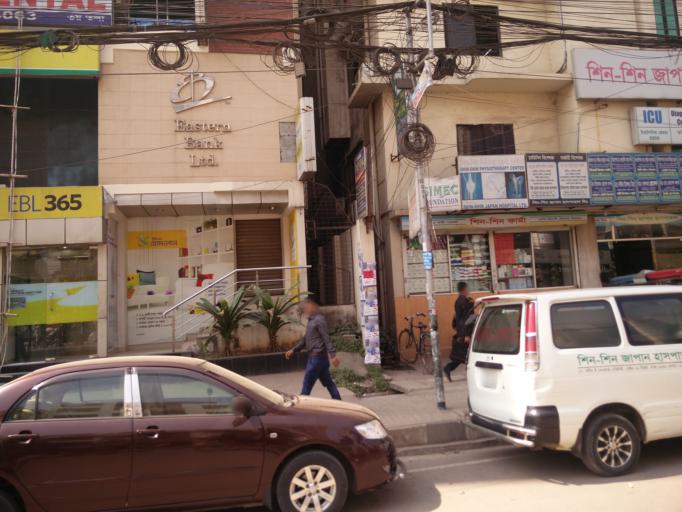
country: BD
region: Dhaka
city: Tungi
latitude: 23.8771
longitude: 90.3908
